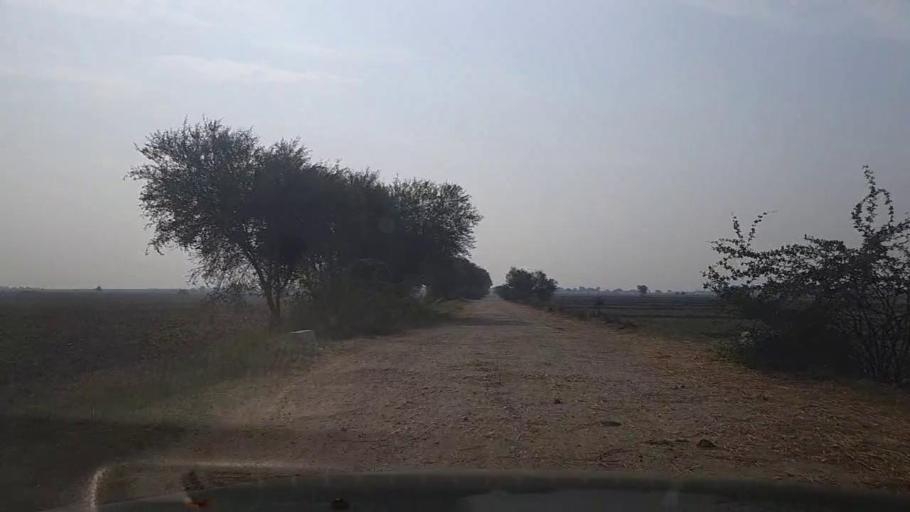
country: PK
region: Sindh
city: Bulri
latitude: 25.0197
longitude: 68.2994
